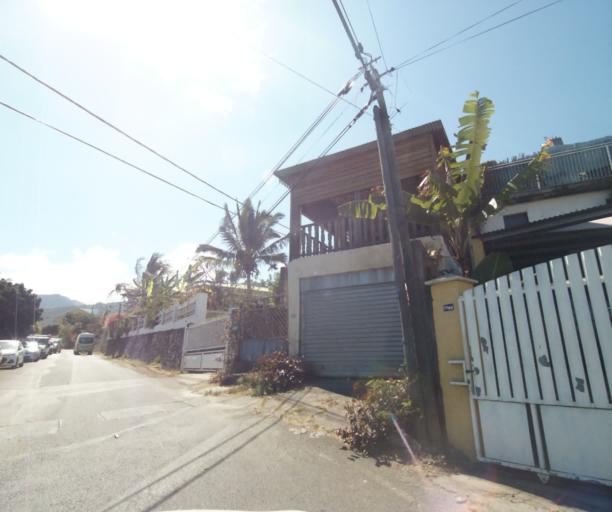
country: RE
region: Reunion
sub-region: Reunion
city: Saint-Paul
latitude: -20.9877
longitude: 55.3235
